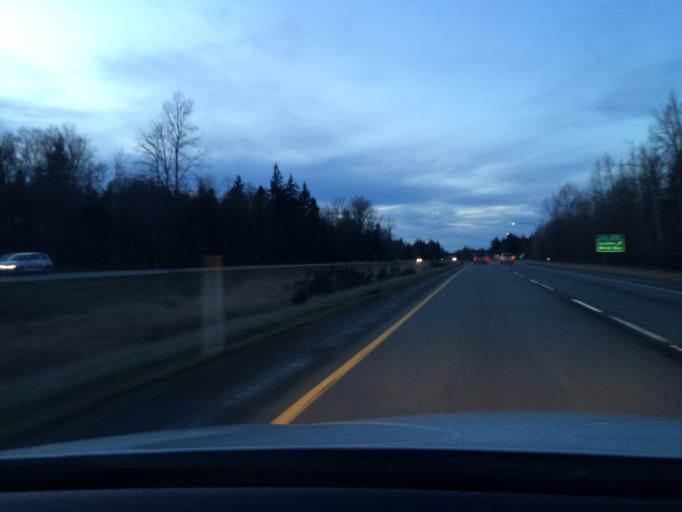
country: US
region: Washington
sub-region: Whatcom County
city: Birch Bay
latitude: 48.9323
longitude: -122.6550
